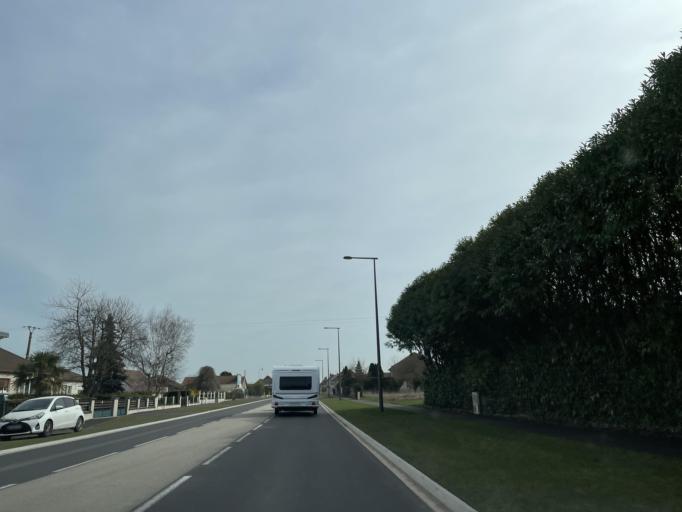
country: FR
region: Champagne-Ardenne
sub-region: Departement de l'Aube
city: Romilly-sur-Seine
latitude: 48.5138
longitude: 3.6348
